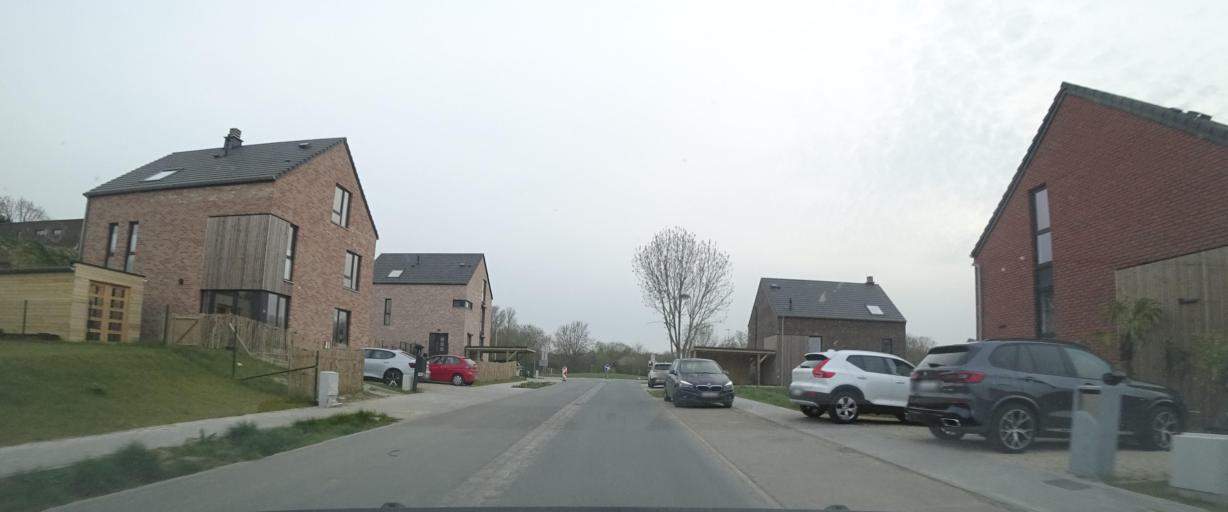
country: BE
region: Wallonia
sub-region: Province du Brabant Wallon
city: Ottignies
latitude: 50.6796
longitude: 4.5539
